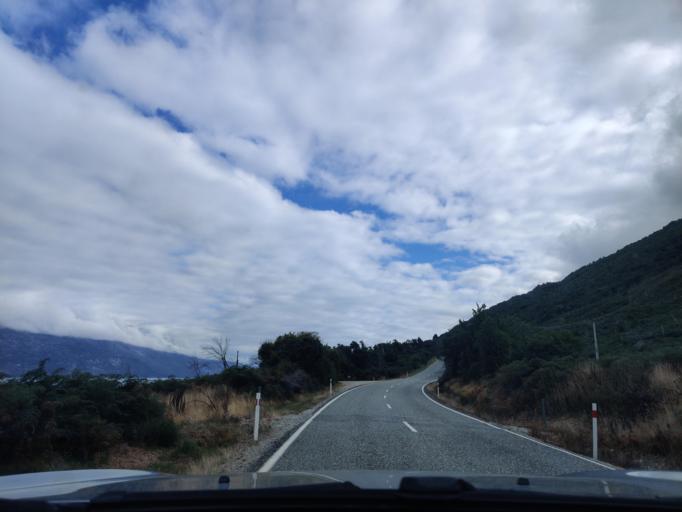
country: NZ
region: Otago
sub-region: Queenstown-Lakes District
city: Queenstown
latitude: -45.0759
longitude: 168.4658
